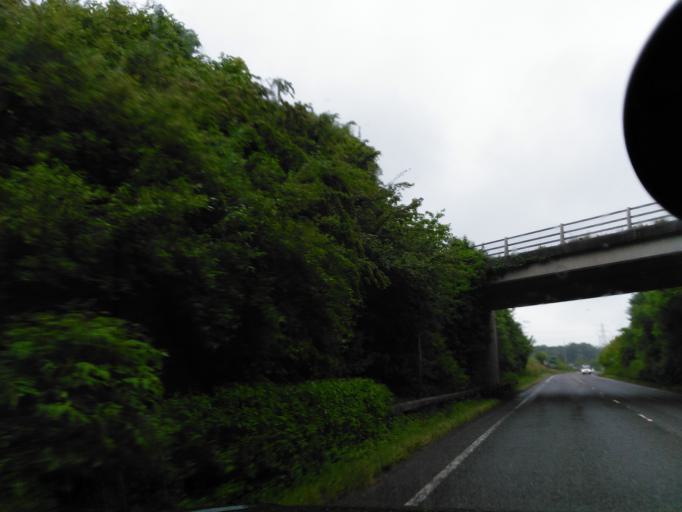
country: GB
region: England
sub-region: Somerset
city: Frome
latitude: 51.2467
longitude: -2.2895
